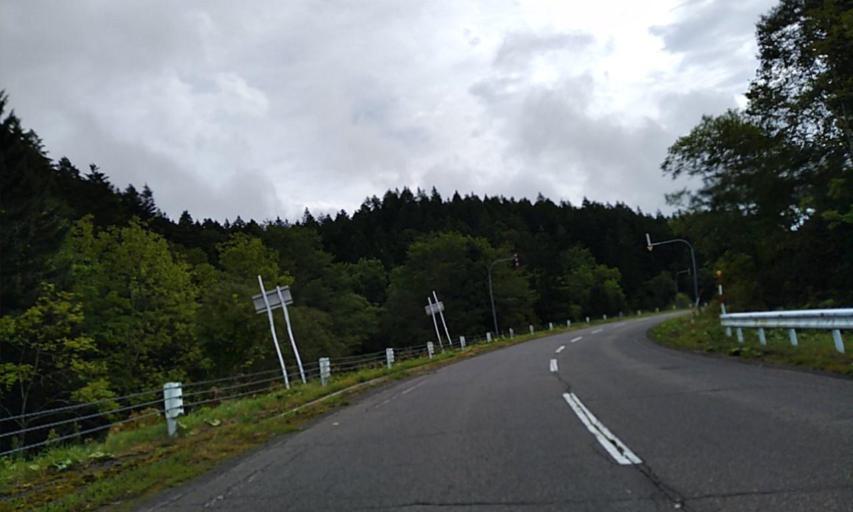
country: JP
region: Hokkaido
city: Abashiri
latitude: 43.6255
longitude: 144.5750
